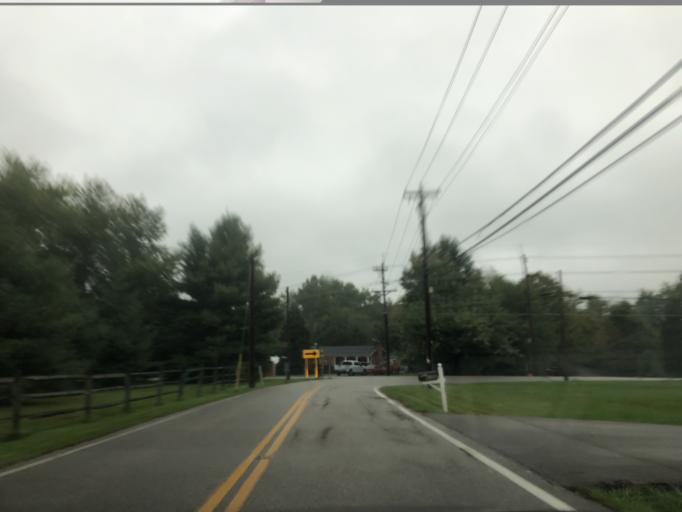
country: US
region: Ohio
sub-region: Clermont County
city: Mulberry
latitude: 39.2122
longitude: -84.2448
